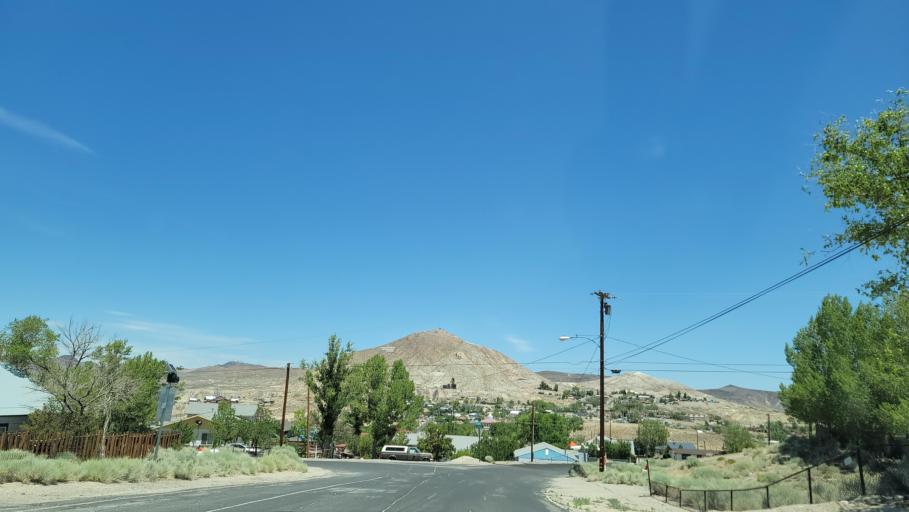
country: US
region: Nevada
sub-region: Nye County
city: Tonopah
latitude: 38.0612
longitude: -117.2312
